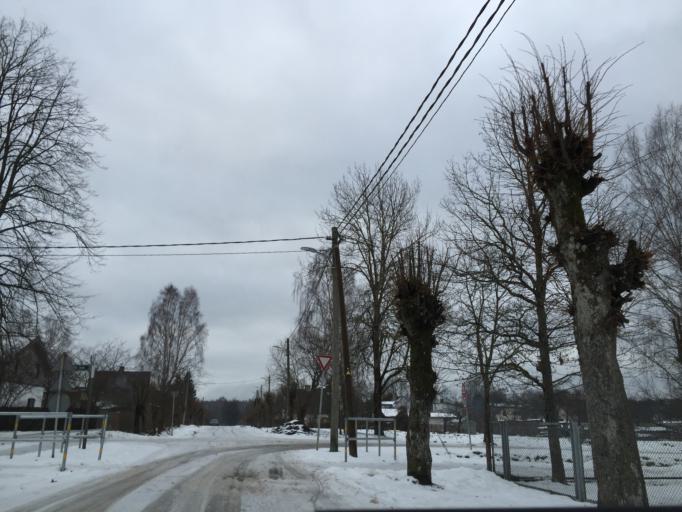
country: LV
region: Saulkrastu
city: Saulkrasti
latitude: 57.2610
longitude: 24.4188
